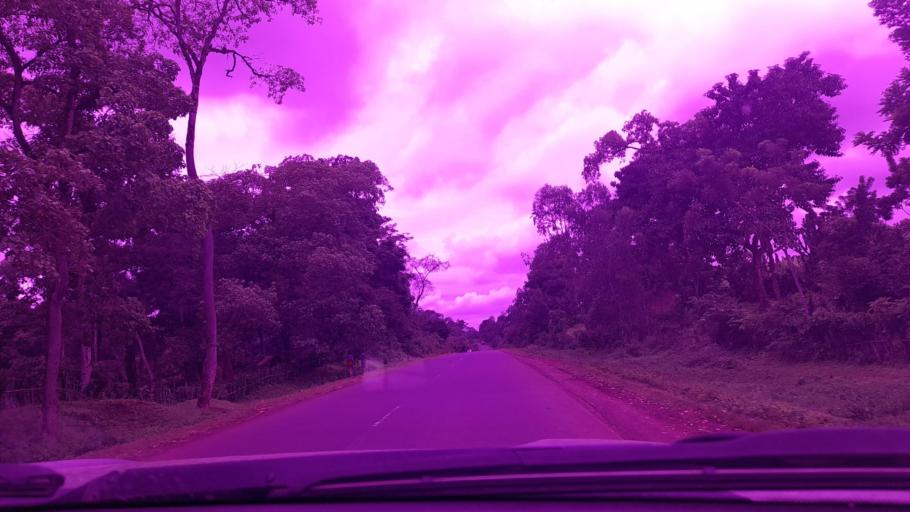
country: ET
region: Southern Nations, Nationalities, and People's Region
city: Bonga
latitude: 7.2797
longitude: 35.9508
